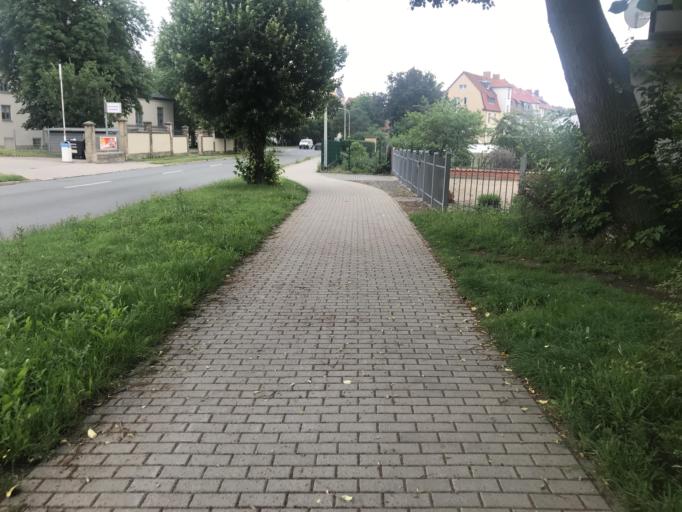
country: DE
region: Saxony-Anhalt
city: Quedlinburg
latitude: 51.7945
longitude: 11.1381
